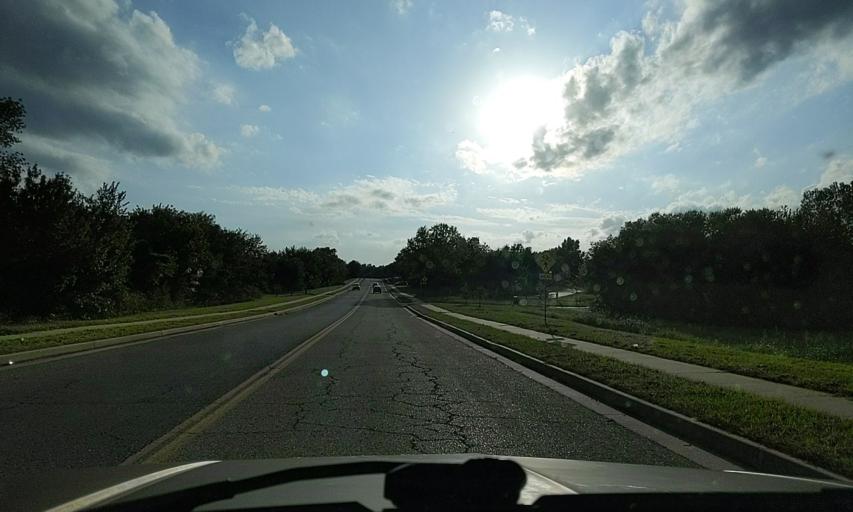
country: US
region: Oklahoma
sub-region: Tulsa County
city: Tulsa
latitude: 36.1954
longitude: -95.9797
